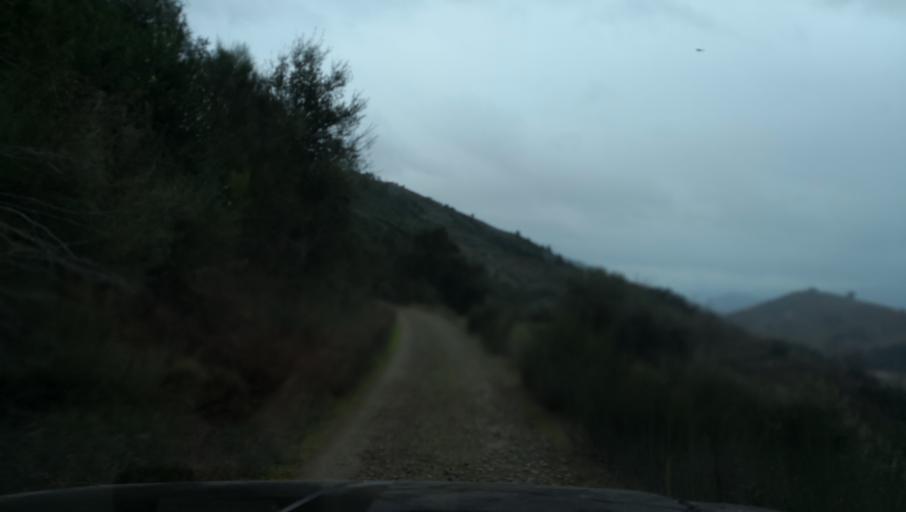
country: PT
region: Vila Real
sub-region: Vila Real
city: Vila Real
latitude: 41.2595
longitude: -7.7455
